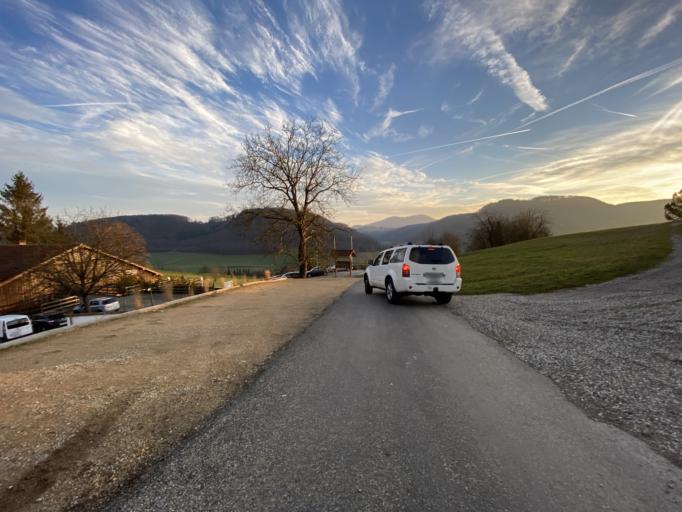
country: CH
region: Aargau
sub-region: Bezirk Laufenburg
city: Frick
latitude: 47.5072
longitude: 8.0405
